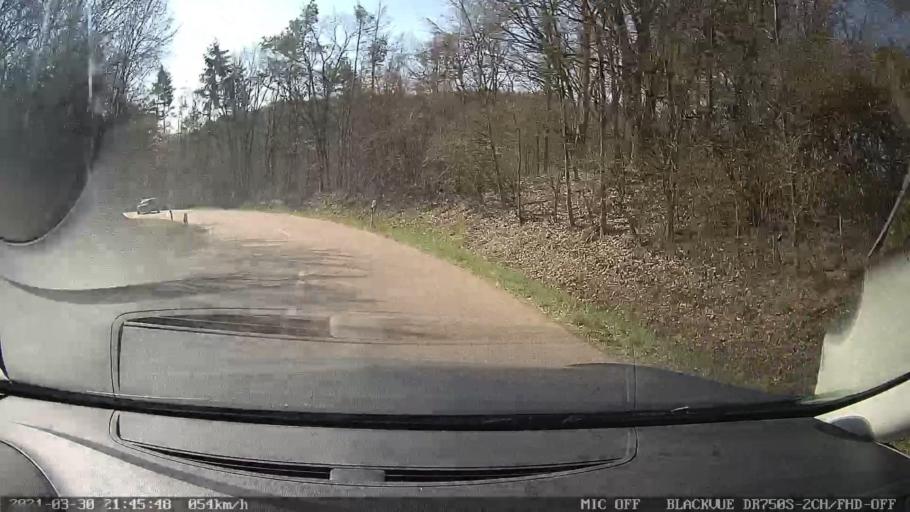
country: DE
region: Bavaria
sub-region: Upper Palatinate
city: Zeitlarn
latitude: 49.0903
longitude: 12.1029
